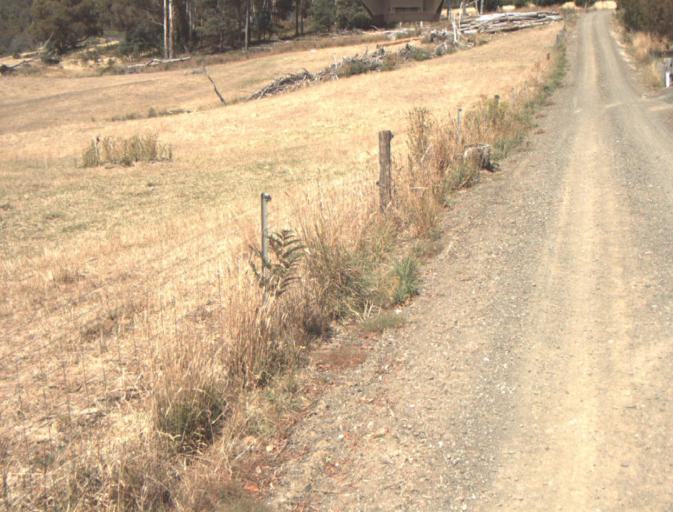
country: AU
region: Tasmania
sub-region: Launceston
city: Mayfield
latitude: -41.2654
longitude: 147.1489
